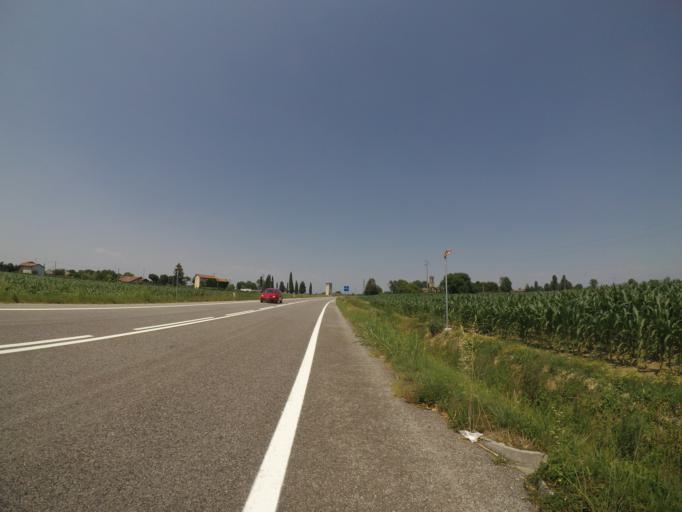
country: IT
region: Friuli Venezia Giulia
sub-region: Provincia di Udine
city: Varmo
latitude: 45.9043
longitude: 13.0043
